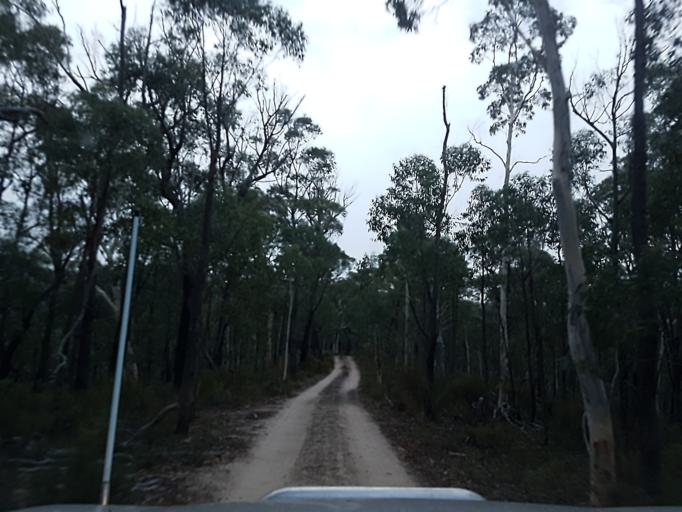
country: AU
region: New South Wales
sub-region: Snowy River
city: Jindabyne
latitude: -36.8617
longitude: 148.2354
